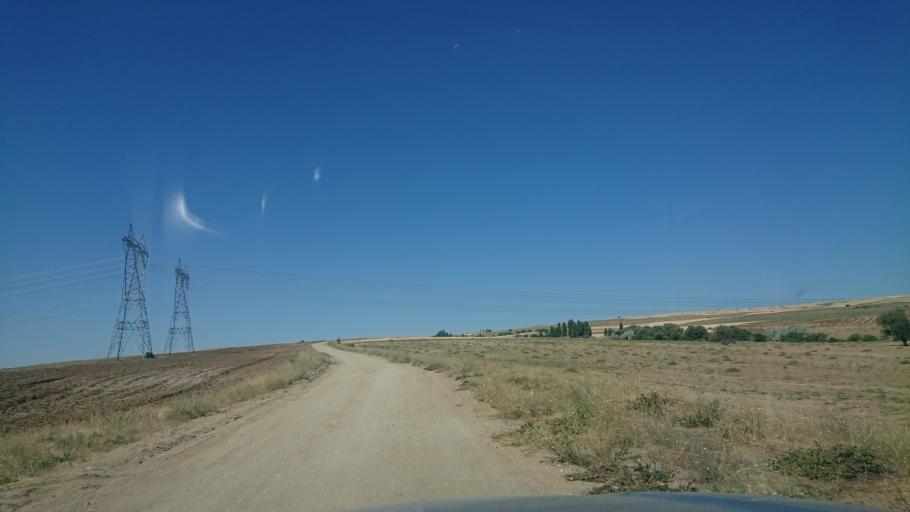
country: TR
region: Aksaray
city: Sariyahsi
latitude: 38.9401
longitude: 33.8702
